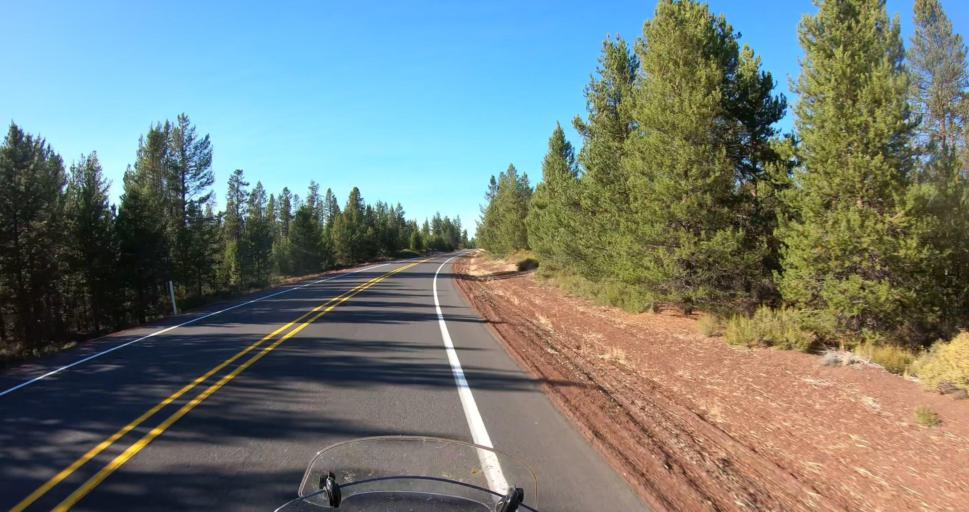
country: US
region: Oregon
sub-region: Deschutes County
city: La Pine
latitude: 43.4564
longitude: -121.3781
